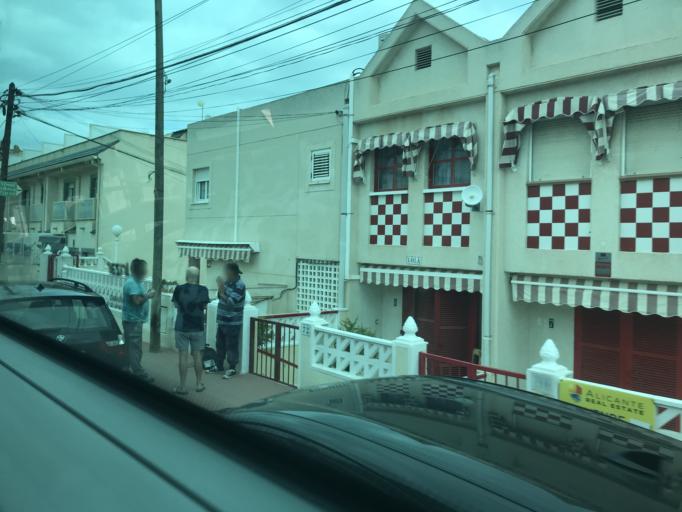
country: ES
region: Valencia
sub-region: Provincia de Alicante
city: Torrevieja
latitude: 38.0219
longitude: -0.6542
